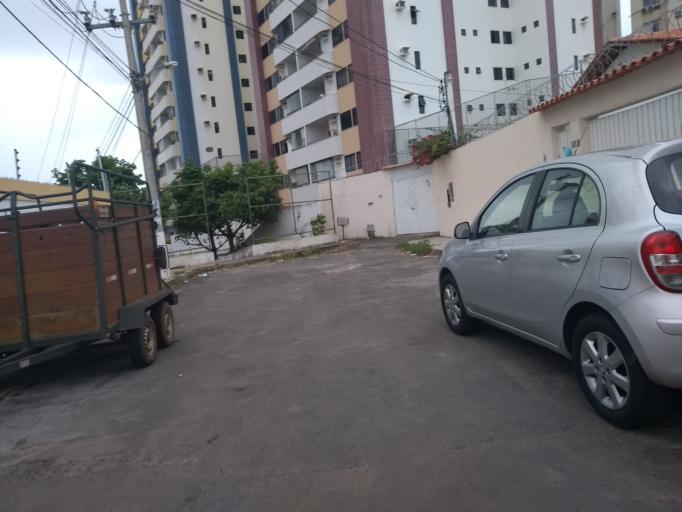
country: BR
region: Bahia
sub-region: Salvador
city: Salvador
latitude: -12.9848
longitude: -38.4434
